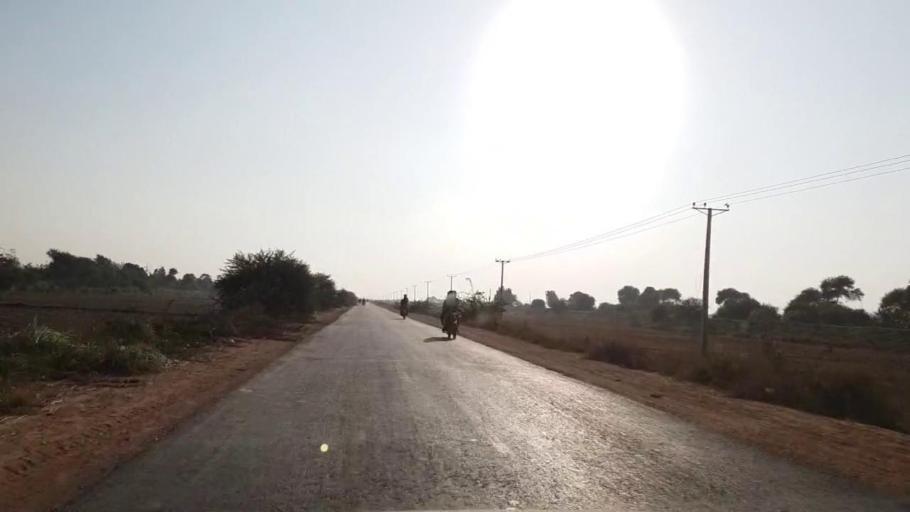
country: PK
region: Sindh
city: Mirpur Batoro
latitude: 24.7647
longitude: 68.2765
